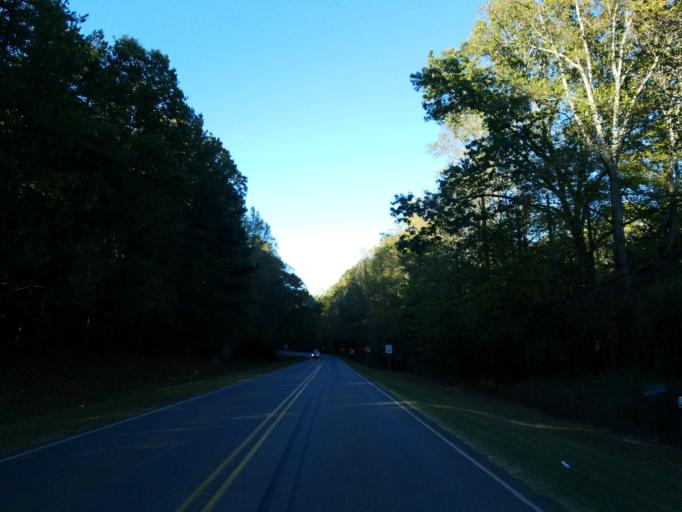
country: US
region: Georgia
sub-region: Pickens County
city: Nelson
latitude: 34.3750
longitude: -84.3718
